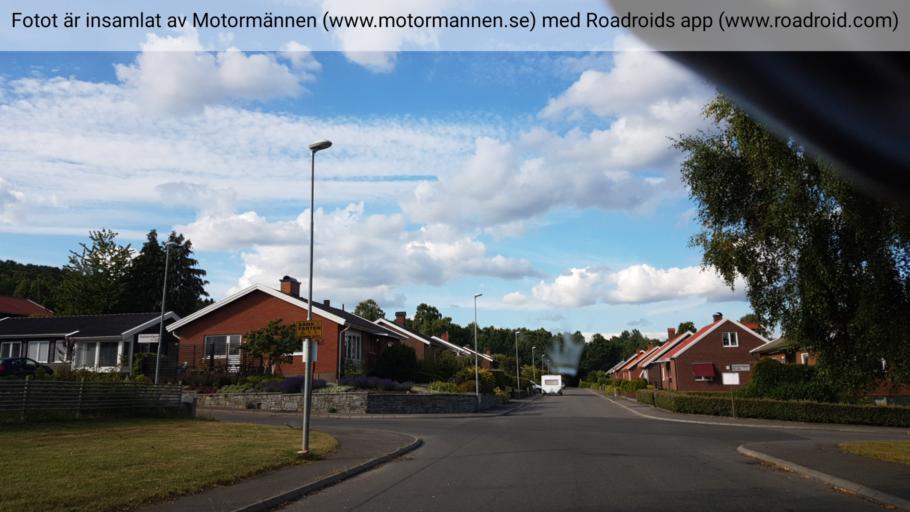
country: SE
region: Vaestra Goetaland
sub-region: Skovde Kommun
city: Skoevde
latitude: 58.3951
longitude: 13.8224
